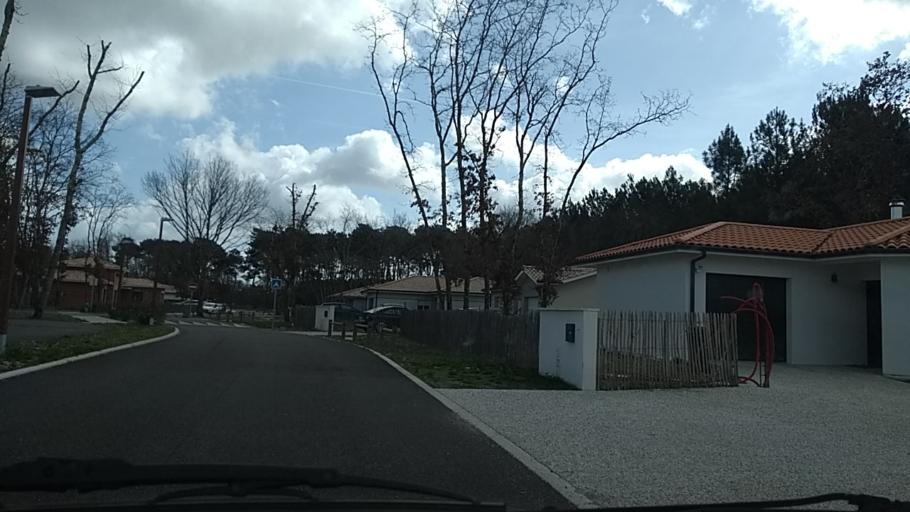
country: FR
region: Aquitaine
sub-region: Departement de la Gironde
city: Salles
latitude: 44.5464
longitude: -0.8767
